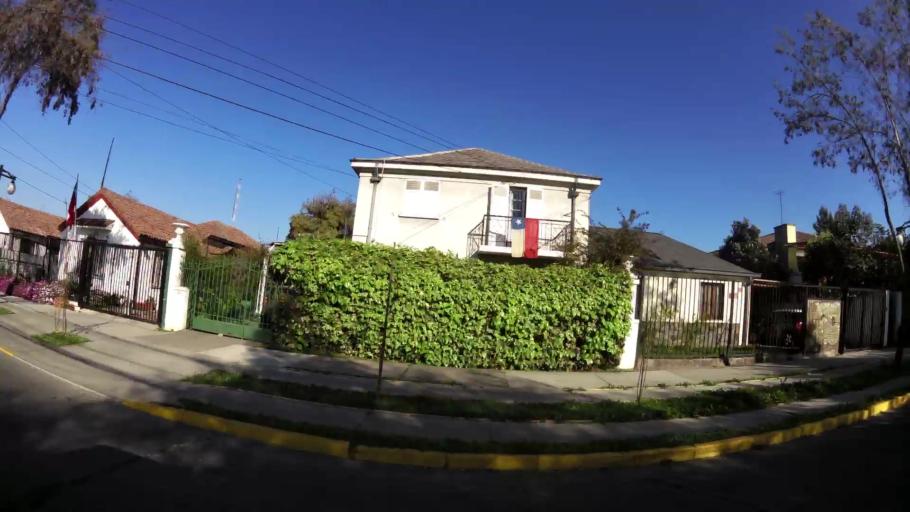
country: CL
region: Santiago Metropolitan
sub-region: Provincia de Santiago
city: Villa Presidente Frei, Nunoa, Santiago, Chile
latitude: -33.4421
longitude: -70.5842
